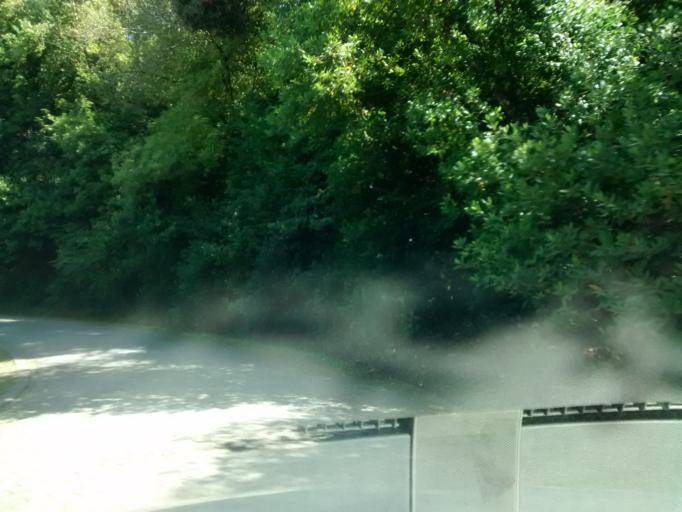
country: PT
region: Aveiro
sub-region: Mealhada
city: Pampilhosa do Botao
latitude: 40.3749
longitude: -8.3654
